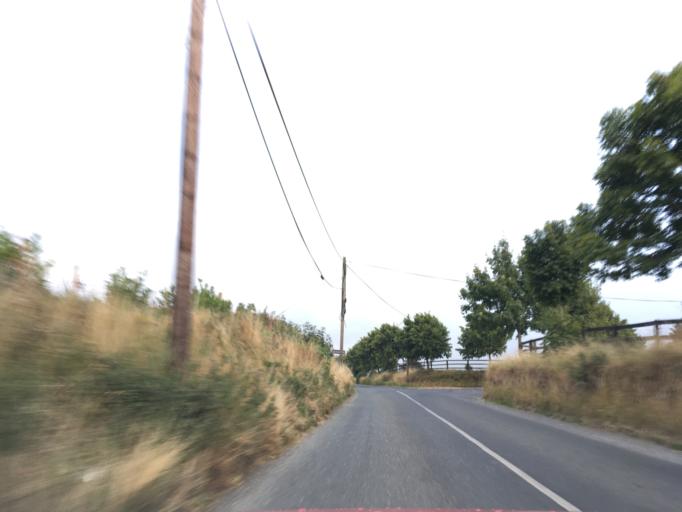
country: IE
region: Munster
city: Cashel
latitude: 52.4957
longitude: -7.9742
